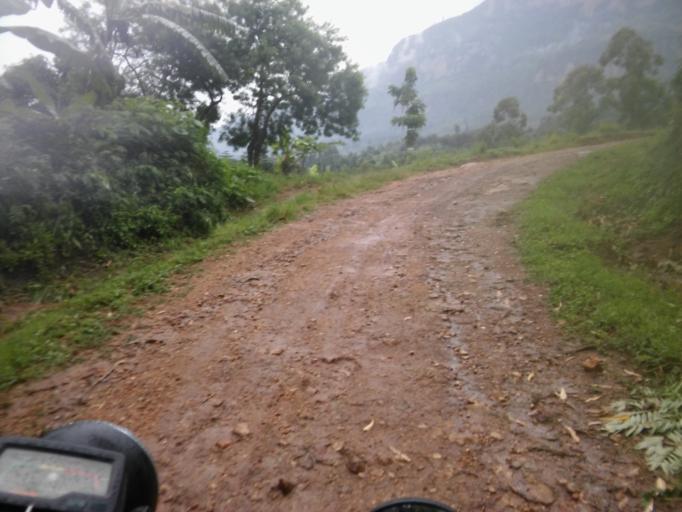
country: UG
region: Eastern Region
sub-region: Bududa District
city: Bududa
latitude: 0.9997
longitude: 34.2370
